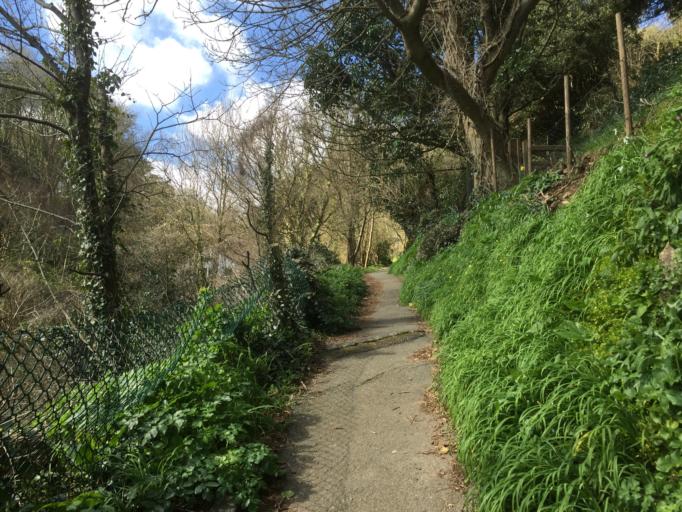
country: GG
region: St Peter Port
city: Saint Peter Port
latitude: 49.4271
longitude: -2.5490
